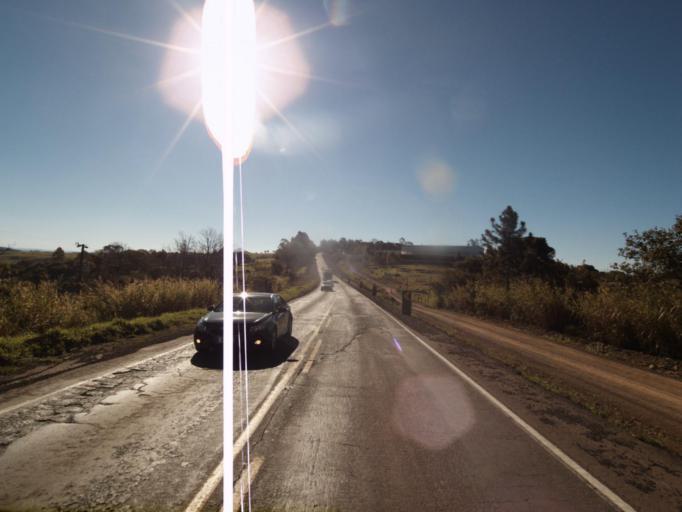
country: AR
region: Misiones
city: Bernardo de Irigoyen
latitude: -26.6774
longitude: -53.5160
